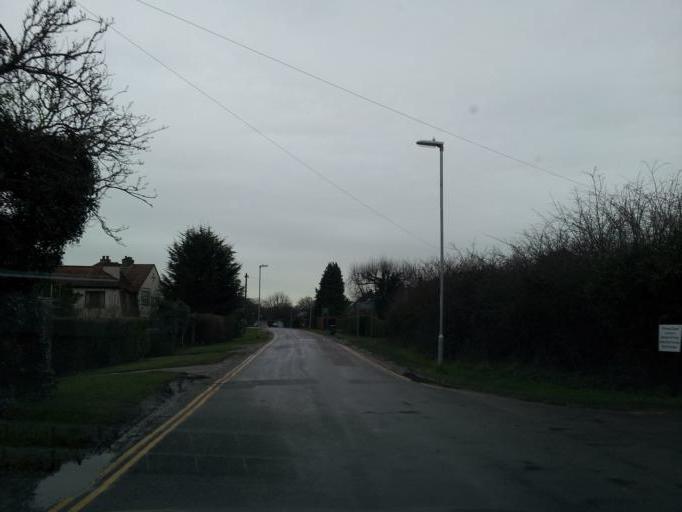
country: GB
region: England
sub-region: Cambridgeshire
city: Cambridge
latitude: 52.1735
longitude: 0.1538
